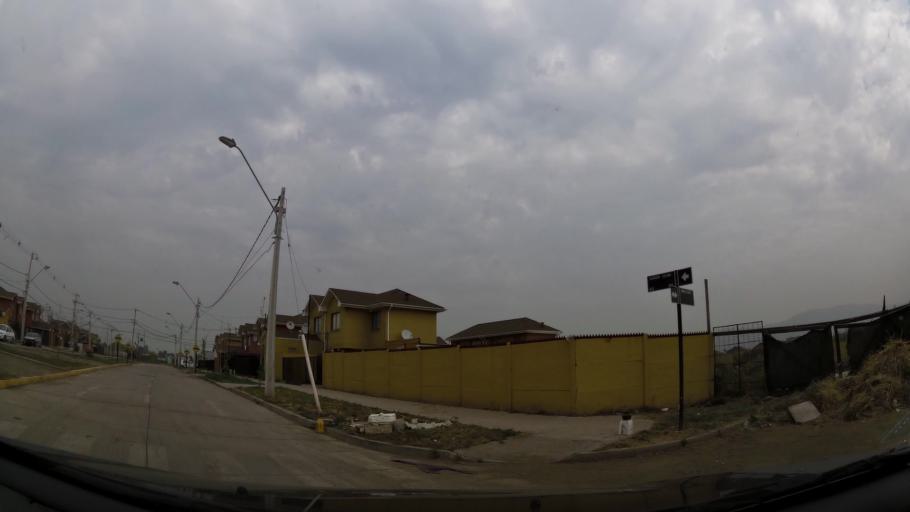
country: CL
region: Santiago Metropolitan
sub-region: Provincia de Chacabuco
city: Chicureo Abajo
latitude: -33.1928
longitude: -70.6804
